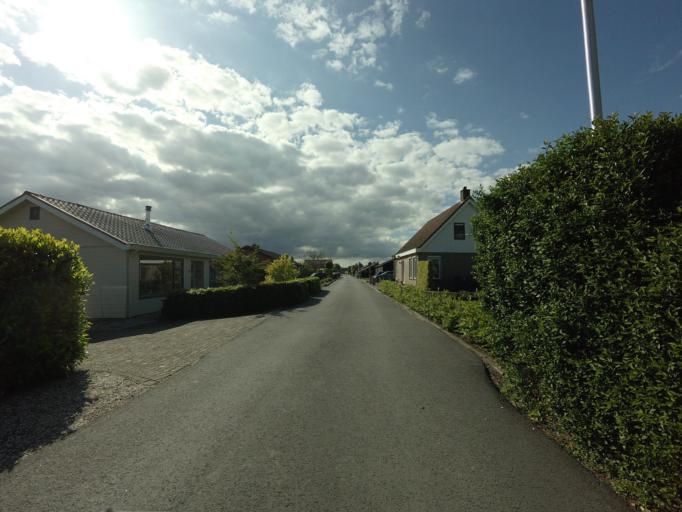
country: NL
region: Utrecht
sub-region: Gemeente Lopik
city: Lopik
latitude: 51.9589
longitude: 4.9834
